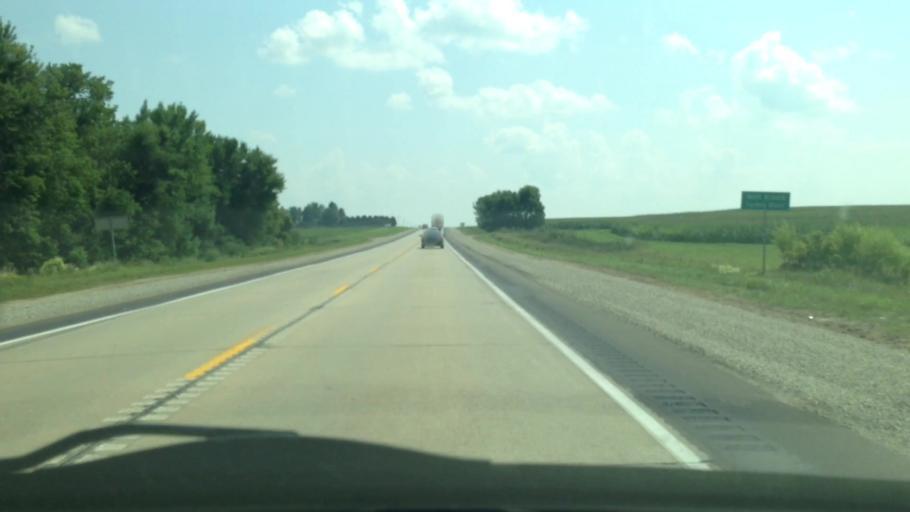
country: US
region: Iowa
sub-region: Howard County
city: Cresco
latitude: 43.3870
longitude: -92.2982
